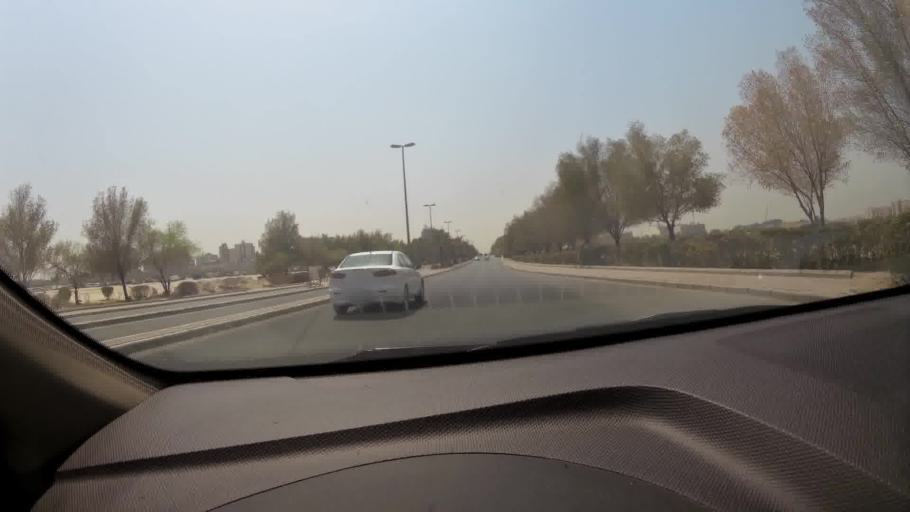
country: KW
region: Al Farwaniyah
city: Al Farwaniyah
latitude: 29.2593
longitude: 47.9483
